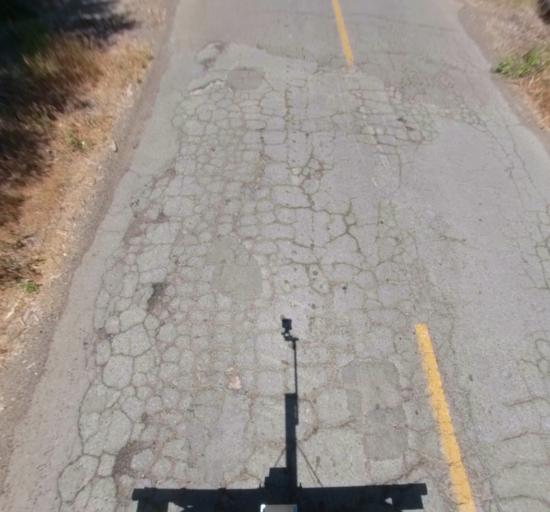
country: US
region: California
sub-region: Madera County
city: Fairmead
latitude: 37.0004
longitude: -120.2742
